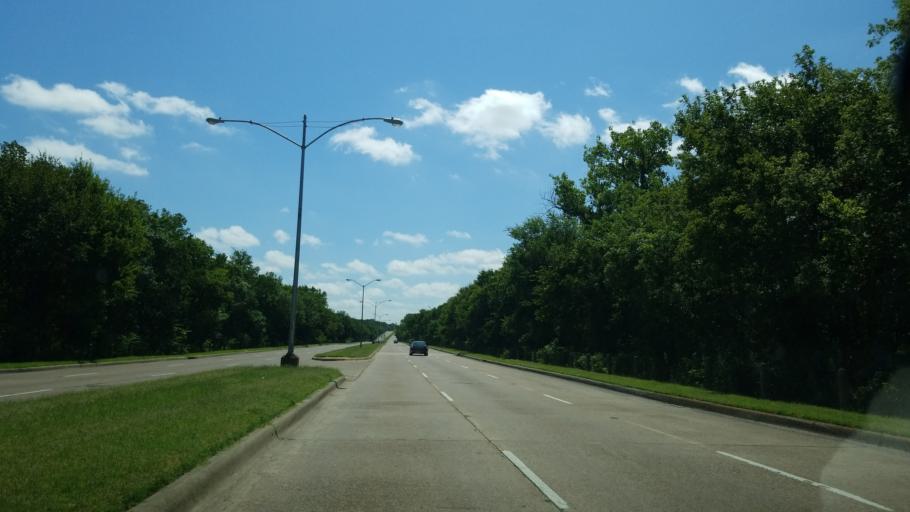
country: US
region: Texas
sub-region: Dallas County
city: Balch Springs
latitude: 32.7492
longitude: -96.7152
